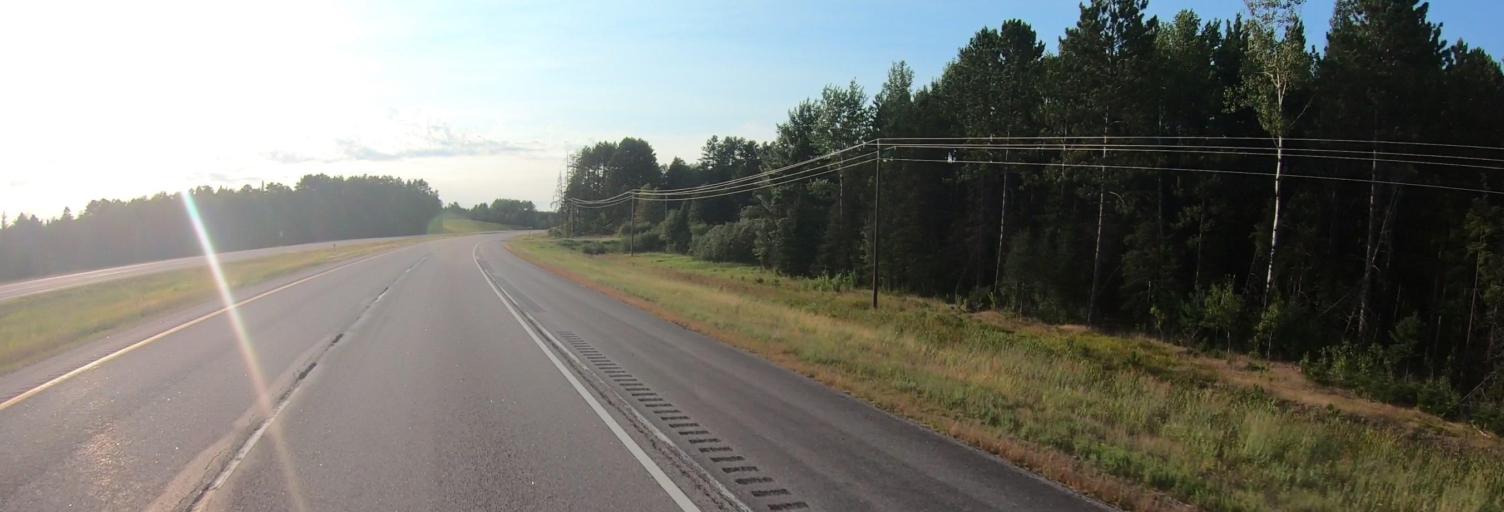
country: US
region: Minnesota
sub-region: Saint Louis County
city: Mountain Iron
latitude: 47.6700
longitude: -92.6309
